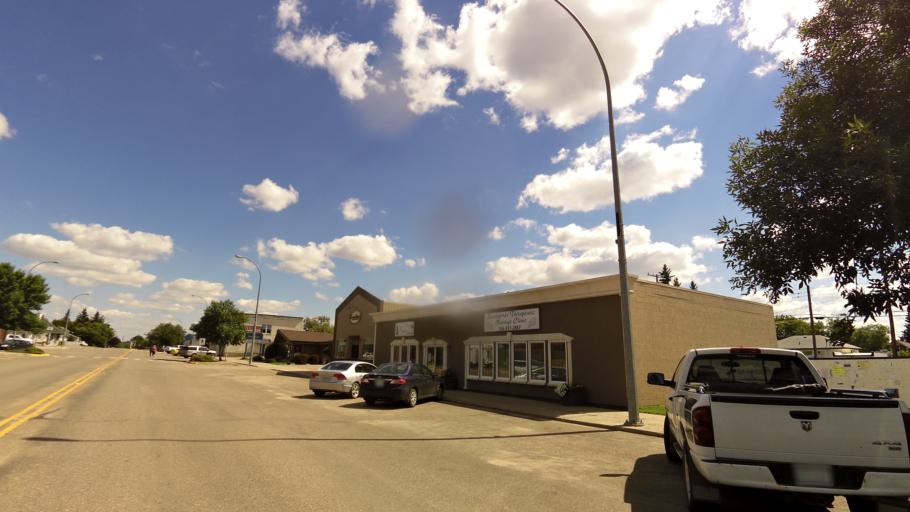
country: CA
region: Saskatchewan
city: North Battleford
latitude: 52.7362
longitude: -108.3074
